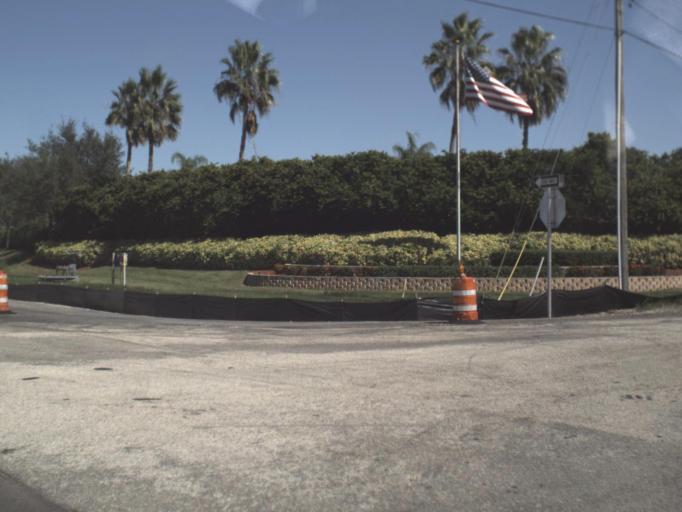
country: US
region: Florida
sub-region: Collier County
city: Lely Resort
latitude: 26.0325
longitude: -81.7005
